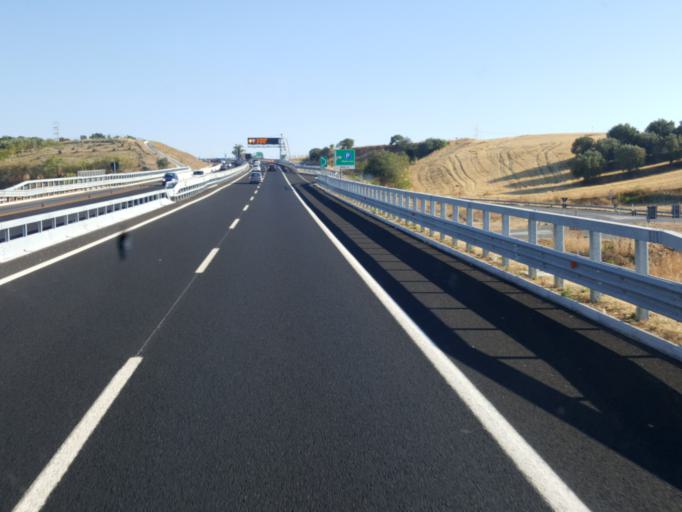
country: IT
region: Latium
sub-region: Citta metropolitana di Roma Capitale
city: Aurelia
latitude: 42.1905
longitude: 11.7863
